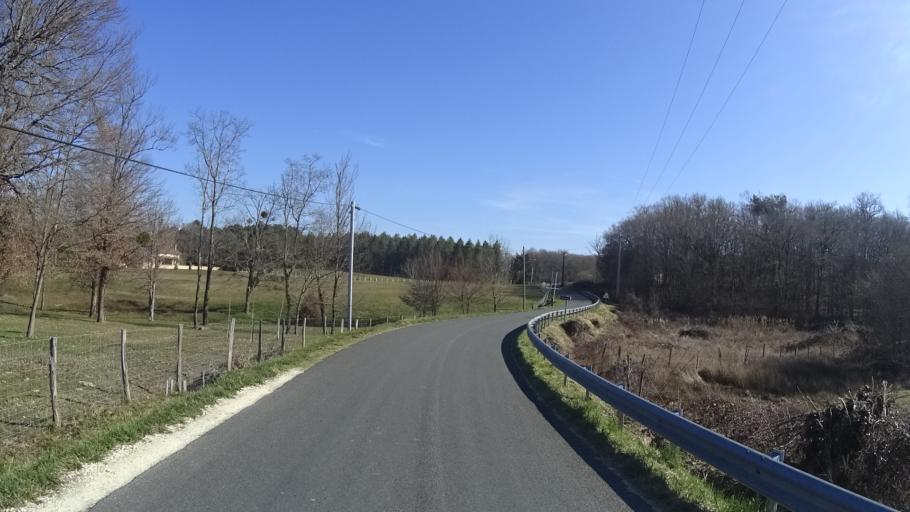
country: FR
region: Aquitaine
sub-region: Departement de la Dordogne
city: Saint-Medard-de-Mussidan
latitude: 45.1293
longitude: 0.2577
